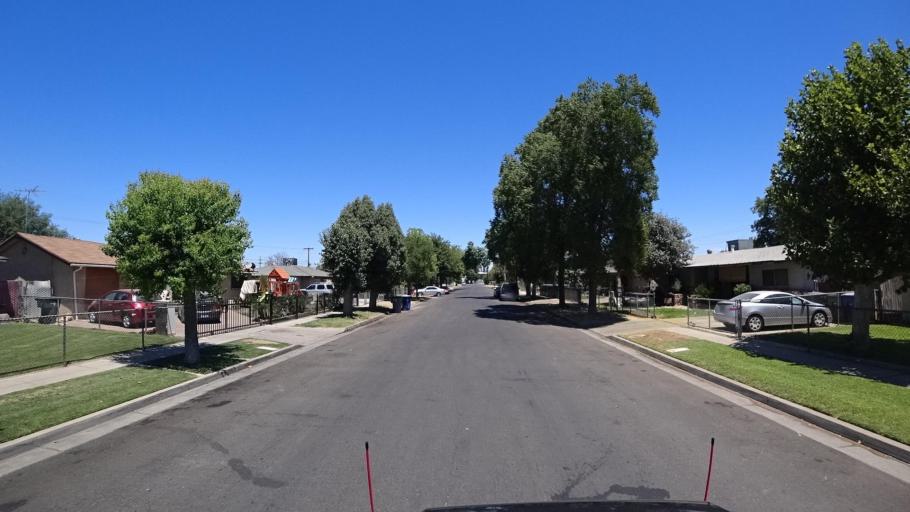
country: US
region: California
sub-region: Fresno County
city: Fresno
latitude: 36.7123
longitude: -119.7511
